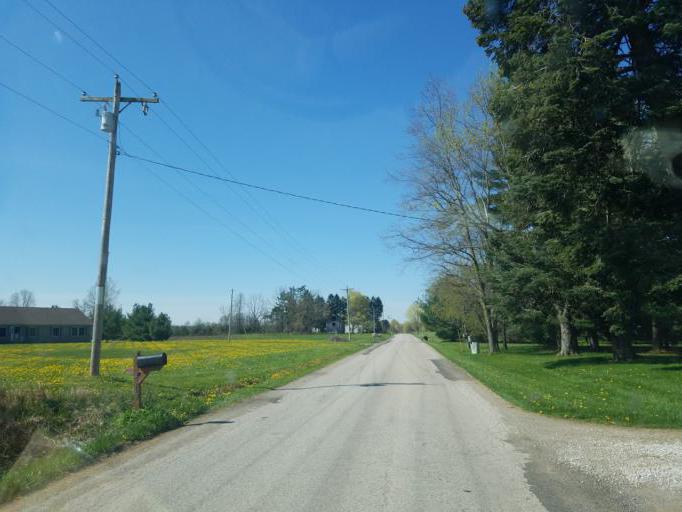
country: US
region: Ohio
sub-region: Morrow County
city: Mount Gilead
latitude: 40.5731
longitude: -82.7978
